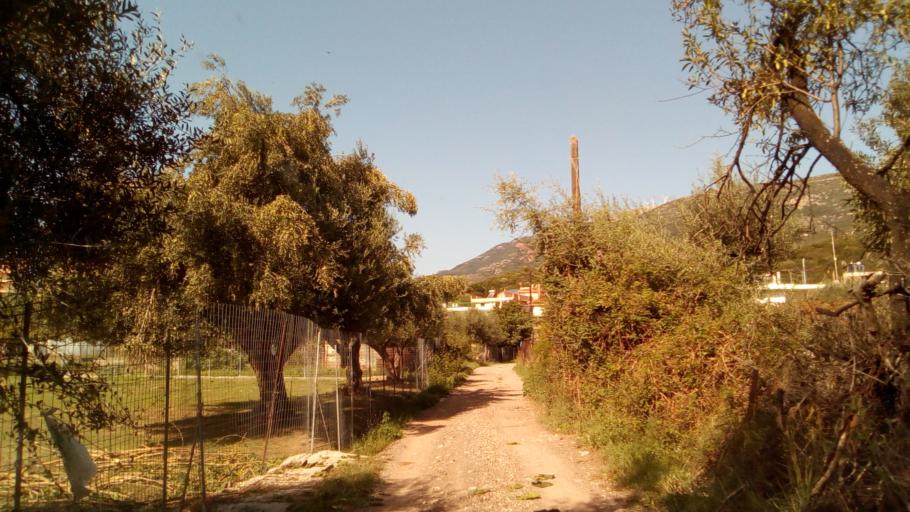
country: GR
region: West Greece
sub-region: Nomos Aitolias kai Akarnanias
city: Nafpaktos
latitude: 38.3915
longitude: 21.8149
